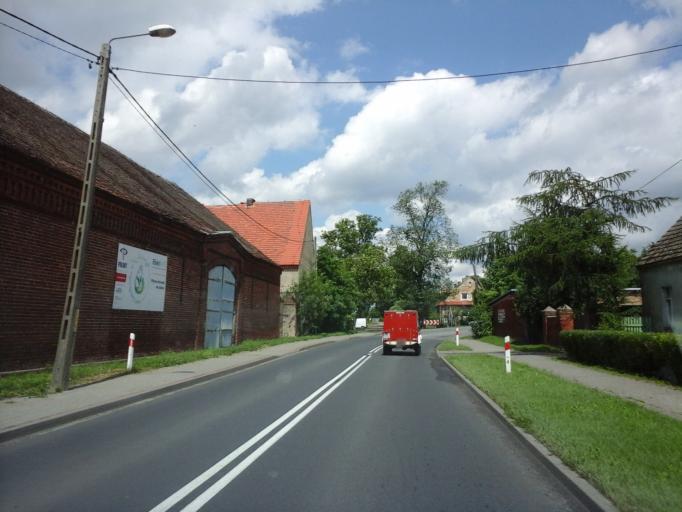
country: PL
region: Lubusz
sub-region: Powiat strzelecko-drezdenecki
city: Strzelce Krajenskie
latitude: 52.9027
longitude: 15.5975
